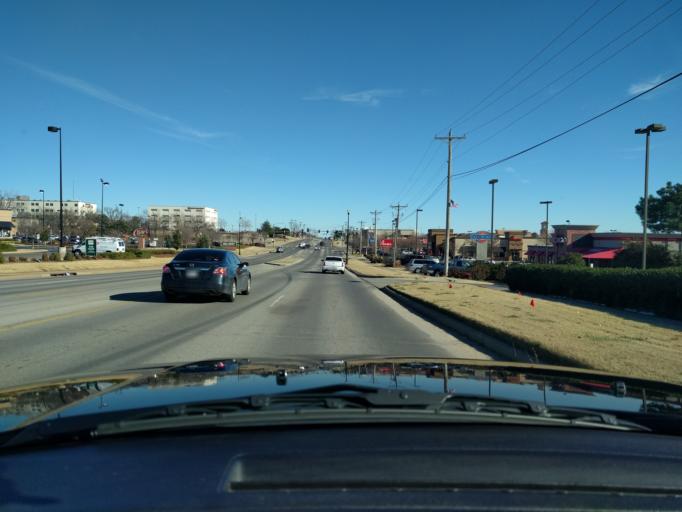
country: US
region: Oklahoma
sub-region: Oklahoma County
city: Edmond
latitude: 35.6527
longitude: -97.4653
